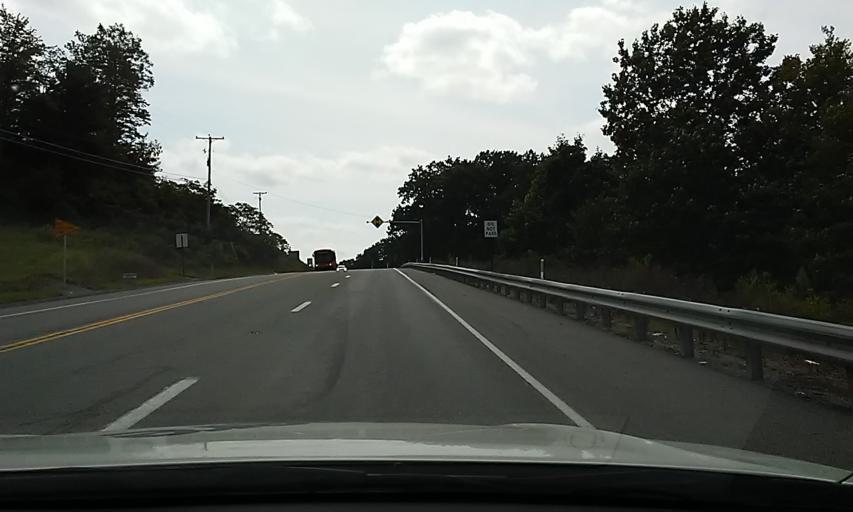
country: US
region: Pennsylvania
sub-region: Jefferson County
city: Punxsutawney
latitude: 40.9312
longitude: -78.9814
